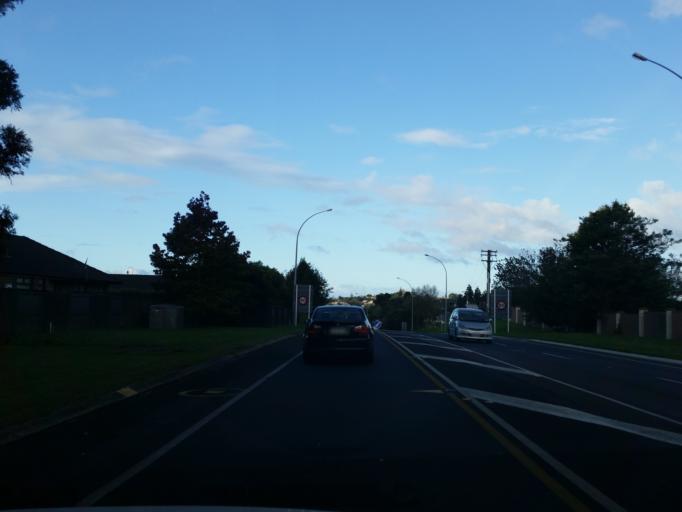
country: NZ
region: Bay of Plenty
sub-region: Tauranga City
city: Tauranga
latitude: -37.6953
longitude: 176.1152
